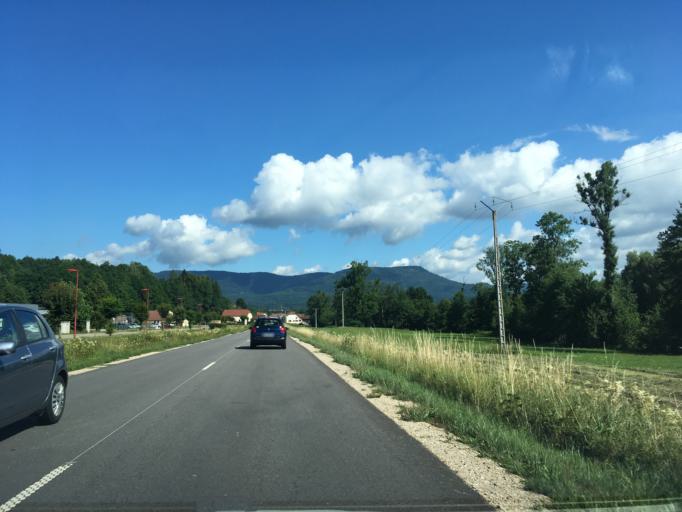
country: FR
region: Lorraine
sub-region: Departement des Vosges
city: Ban-de-Laveline
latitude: 48.2576
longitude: 7.0547
